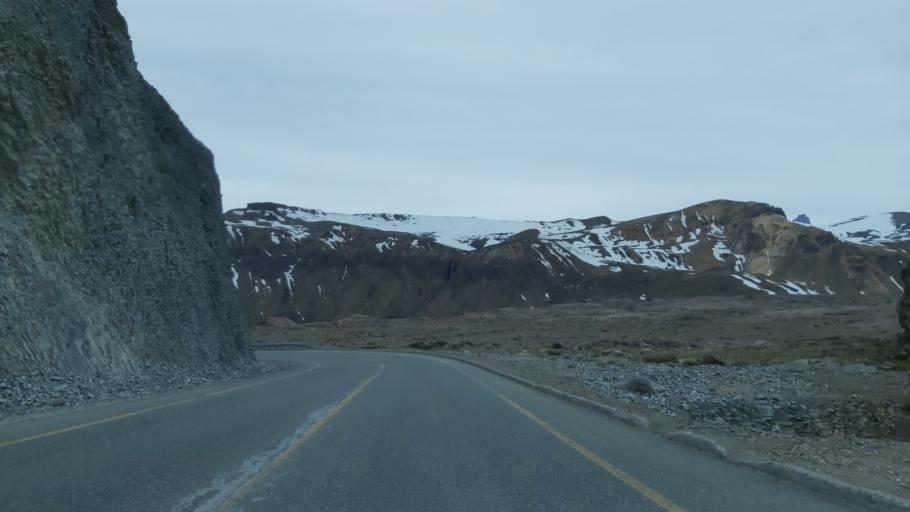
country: CL
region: Maule
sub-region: Provincia de Linares
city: Colbun
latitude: -35.9609
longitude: -70.5732
